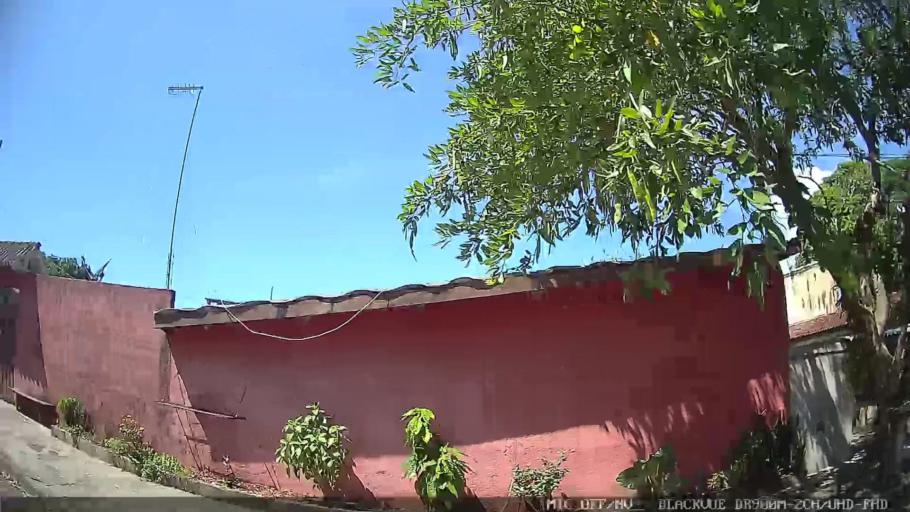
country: BR
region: Sao Paulo
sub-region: Peruibe
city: Peruibe
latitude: -24.3220
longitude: -47.0087
